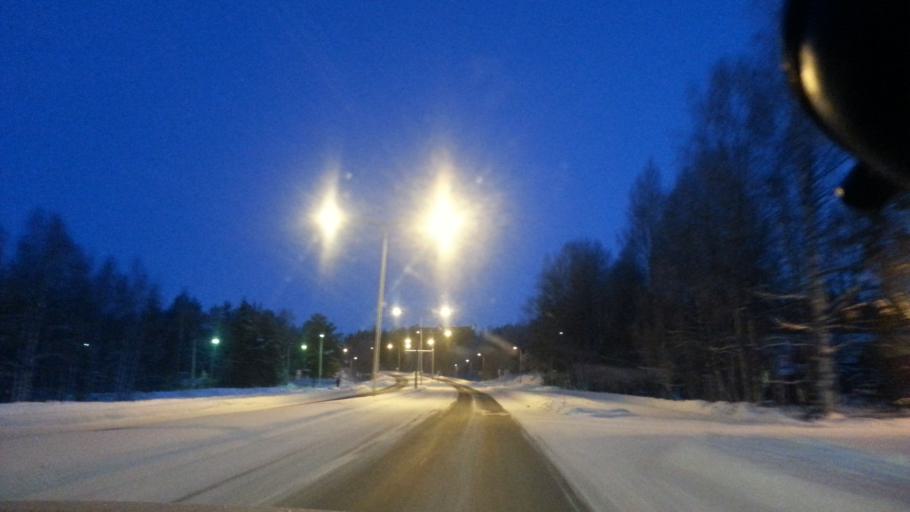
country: FI
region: Lapland
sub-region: Rovaniemi
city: Rovaniemi
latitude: 66.4896
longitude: 25.7553
